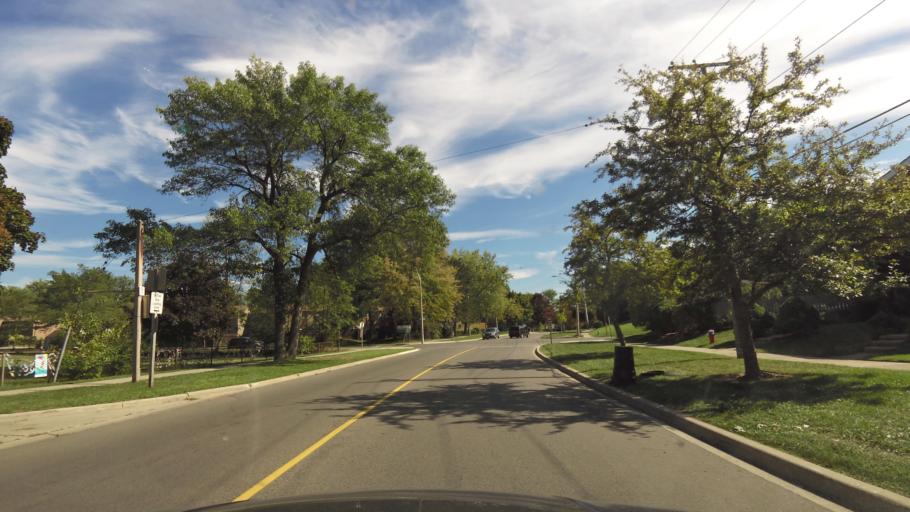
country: CA
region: Ontario
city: Mississauga
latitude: 43.5567
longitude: -79.6544
